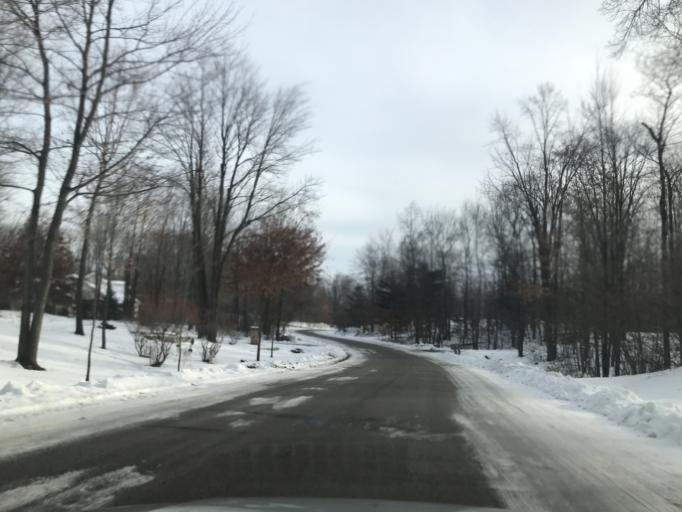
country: US
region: Wisconsin
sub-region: Brown County
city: Suamico
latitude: 44.6888
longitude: -88.0558
